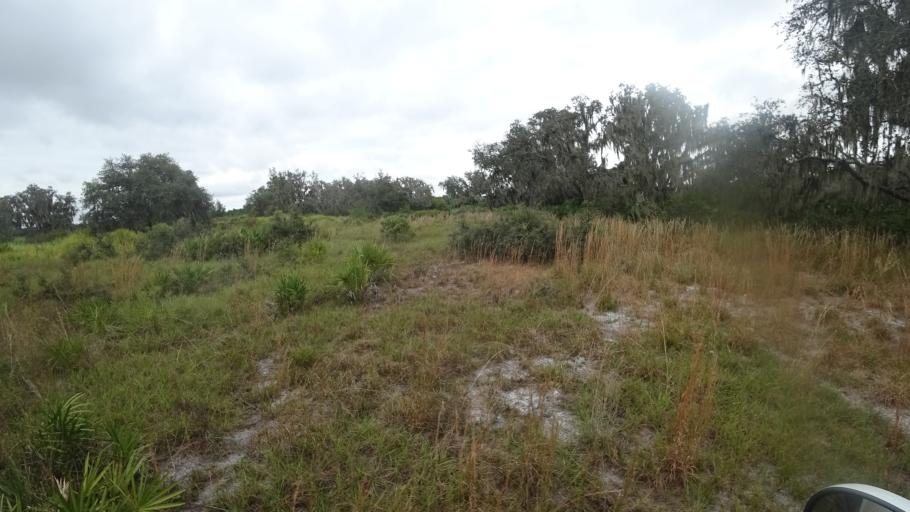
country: US
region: Florida
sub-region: Hillsborough County
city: Wimauma
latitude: 27.5617
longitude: -82.1375
